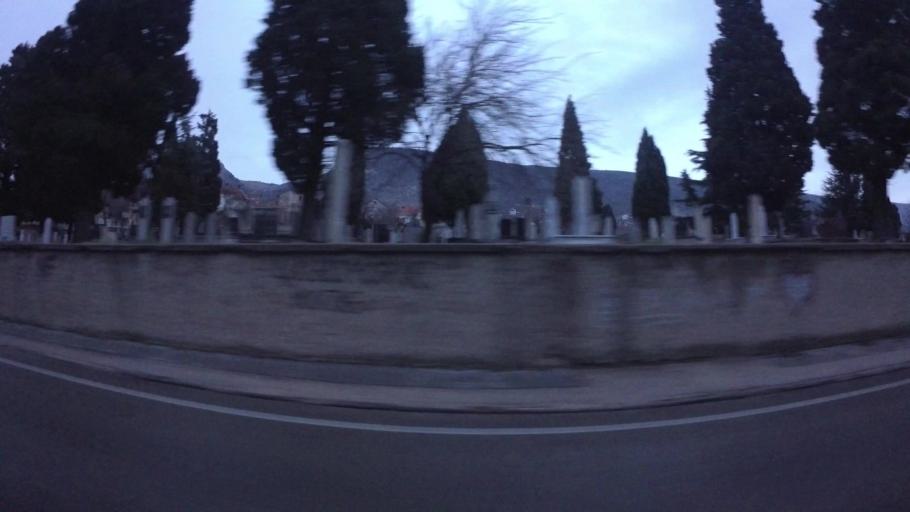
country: BA
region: Federation of Bosnia and Herzegovina
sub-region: Hercegovacko-Bosanski Kanton
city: Mostar
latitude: 43.3313
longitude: 17.8187
